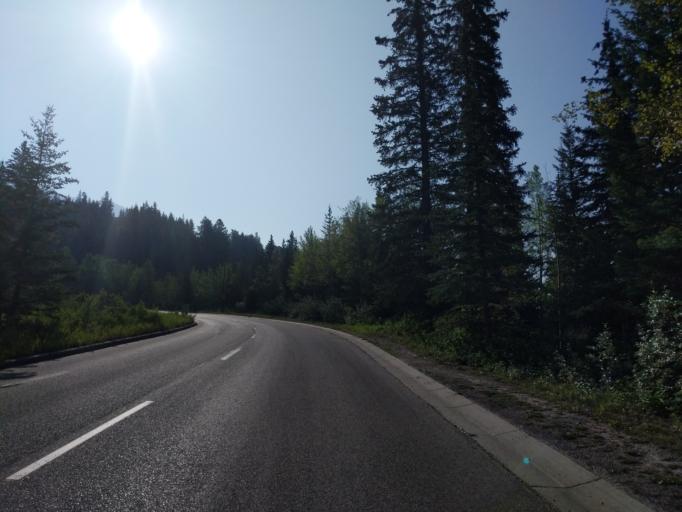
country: CA
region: Alberta
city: Canmore
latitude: 51.0938
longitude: -115.3432
